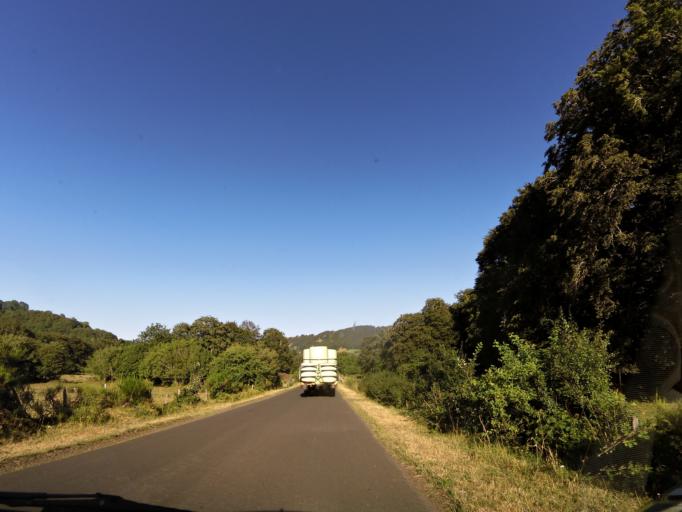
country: FR
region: Auvergne
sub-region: Departement du Puy-de-Dome
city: Mont-Dore
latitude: 45.4401
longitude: 2.9424
